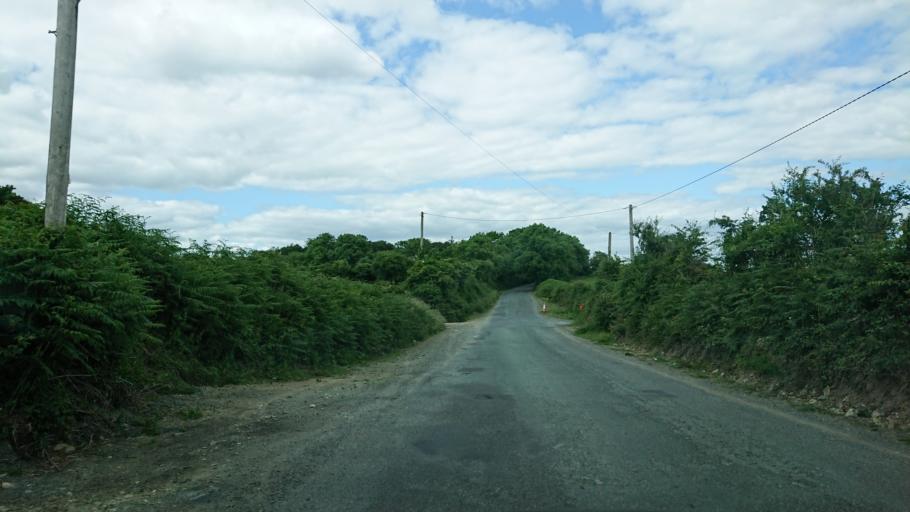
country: IE
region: Munster
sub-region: Waterford
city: Tra Mhor
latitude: 52.2026
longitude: -7.1789
